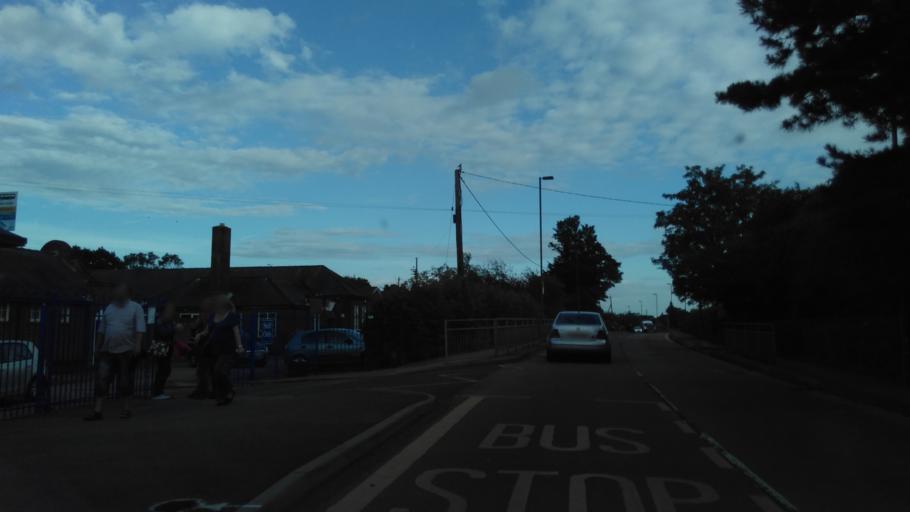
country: GB
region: England
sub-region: Kent
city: Blean
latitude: 51.2990
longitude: 1.0503
